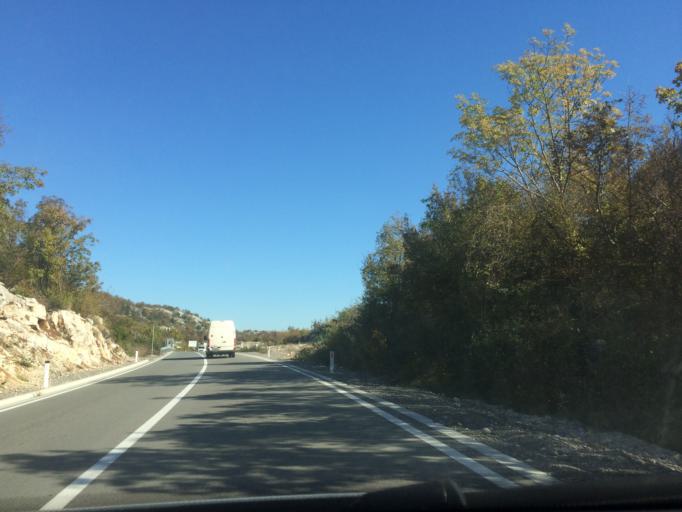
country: ME
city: Mojanovici
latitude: 42.3839
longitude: 19.1042
